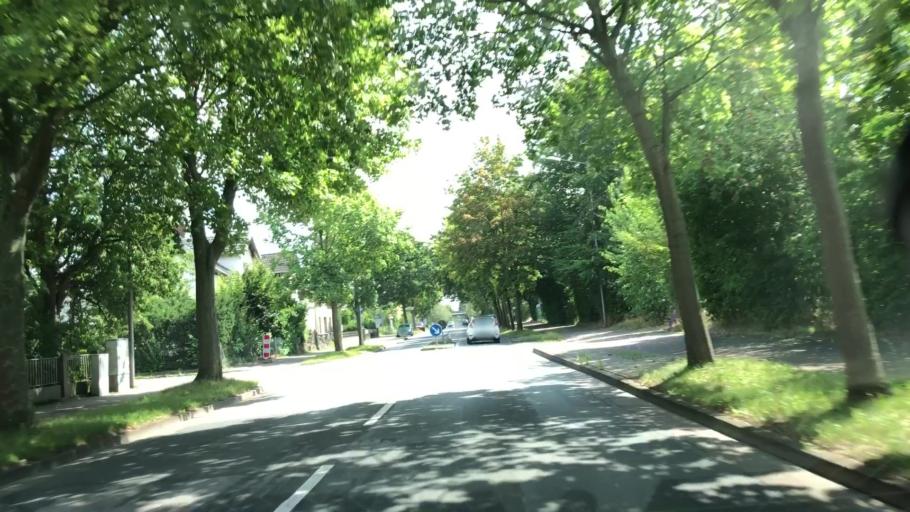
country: DE
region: North Rhine-Westphalia
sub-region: Regierungsbezirk Detmold
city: Minden
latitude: 52.2684
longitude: 8.9040
